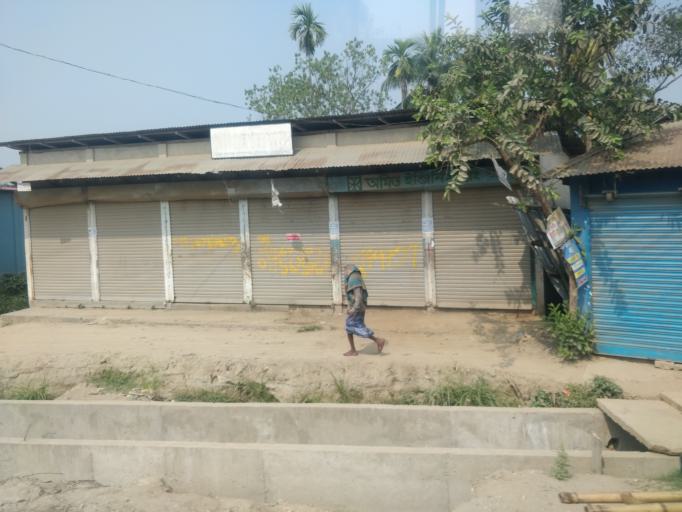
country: BD
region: Sylhet
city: Habiganj
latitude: 24.3657
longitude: 91.4160
